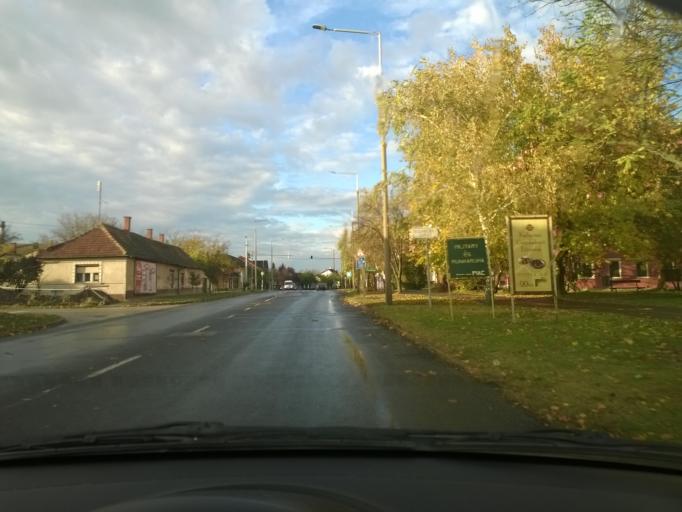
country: HU
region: Bacs-Kiskun
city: Kalocsa
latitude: 46.5326
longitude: 18.9862
